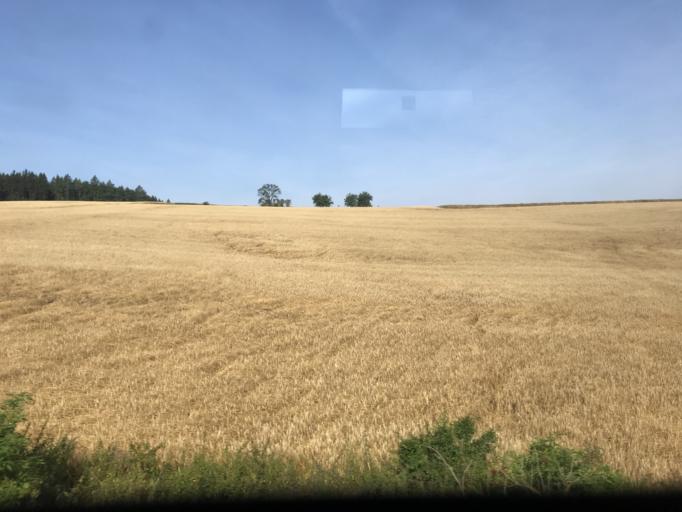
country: CZ
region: Central Bohemia
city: Votice
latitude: 49.5883
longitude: 14.5854
